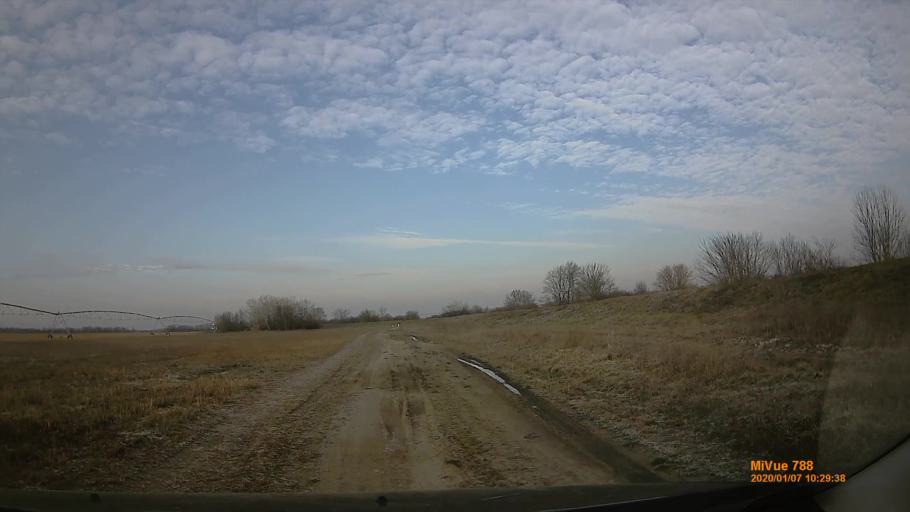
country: HU
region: Gyor-Moson-Sopron
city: Rajka
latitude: 47.9193
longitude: 17.1887
